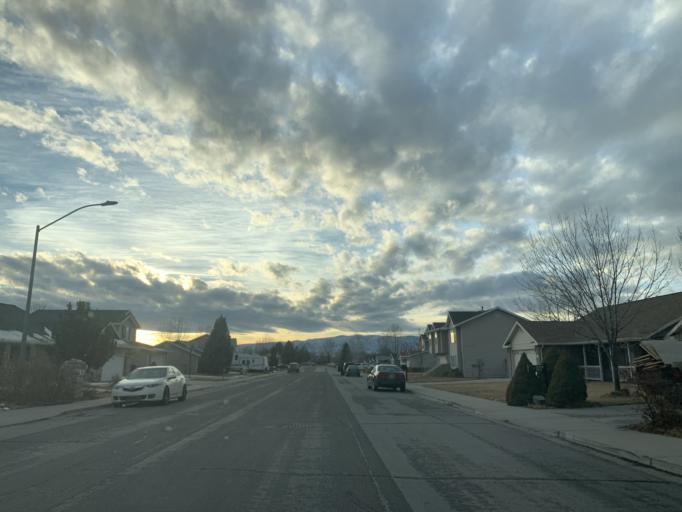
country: US
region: Utah
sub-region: Utah County
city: Orem
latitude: 40.2478
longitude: -111.7084
